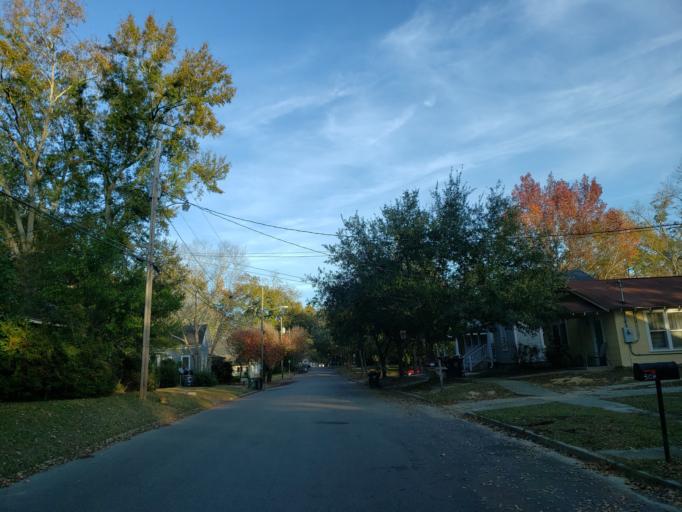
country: US
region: Mississippi
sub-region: Forrest County
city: Hattiesburg
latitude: 31.3302
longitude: -89.2998
